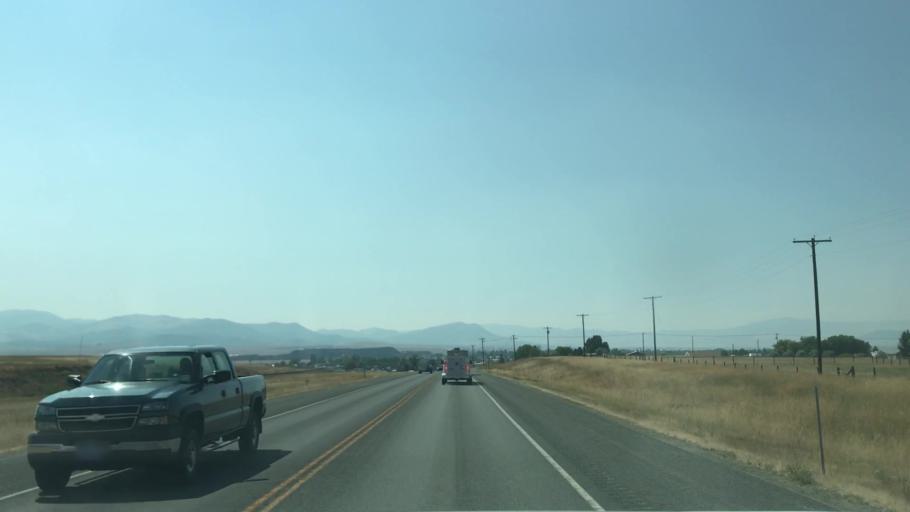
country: US
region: Montana
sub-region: Lewis and Clark County
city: East Helena
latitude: 46.5874
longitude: -111.8847
